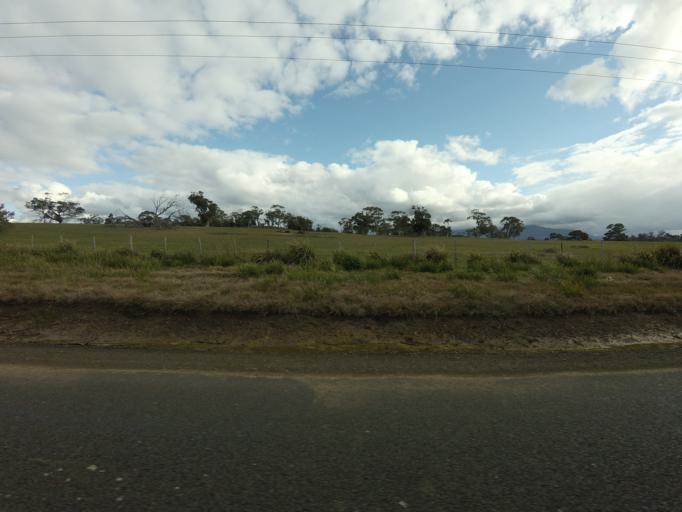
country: AU
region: Tasmania
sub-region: Northern Midlands
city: Evandale
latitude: -41.8724
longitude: 147.2986
